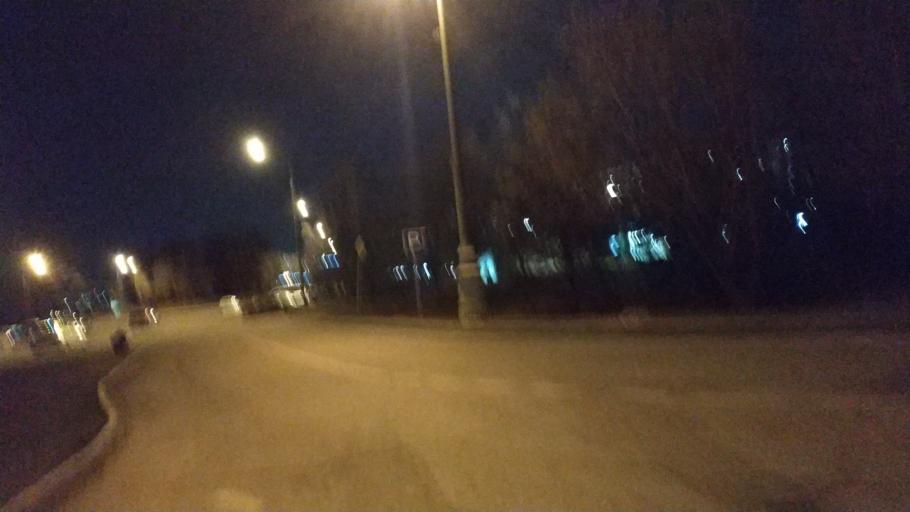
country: RU
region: Moscow
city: Strogino
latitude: 55.8336
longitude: 37.3836
